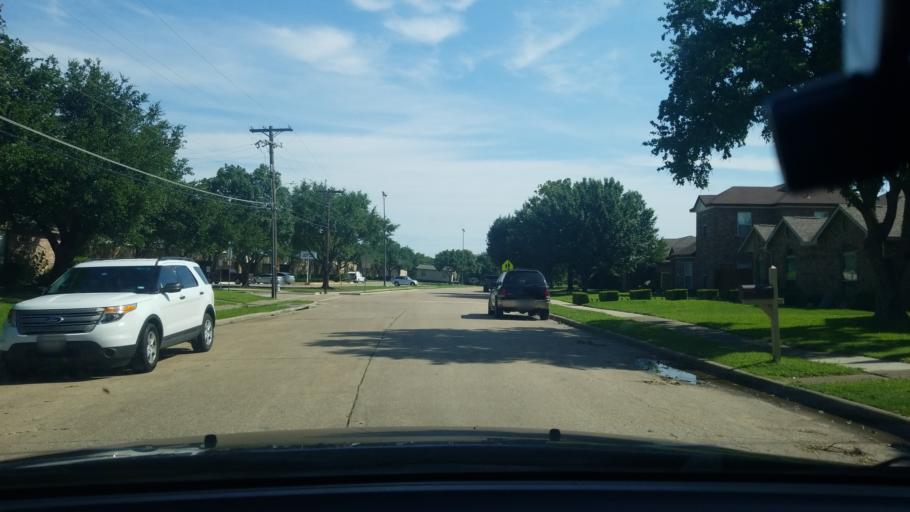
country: US
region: Texas
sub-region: Dallas County
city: Mesquite
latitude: 32.7721
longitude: -96.5801
